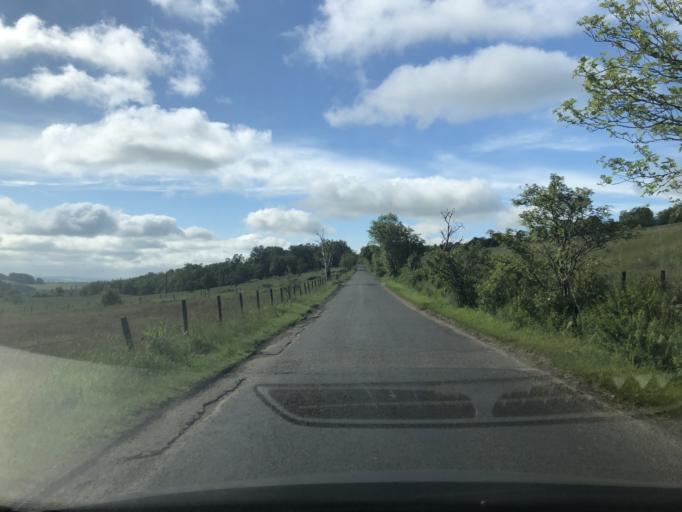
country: GB
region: Scotland
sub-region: Angus
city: Kirriemuir
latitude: 56.7502
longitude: -3.0145
